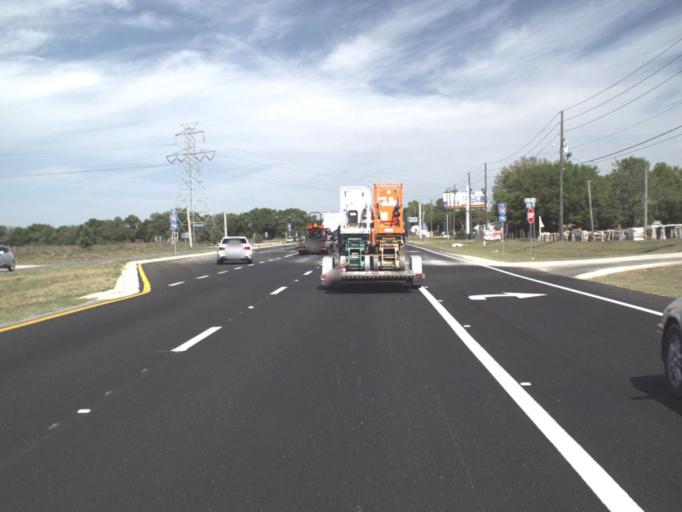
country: US
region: Florida
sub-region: Marion County
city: Belleview
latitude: 29.0287
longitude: -82.0215
